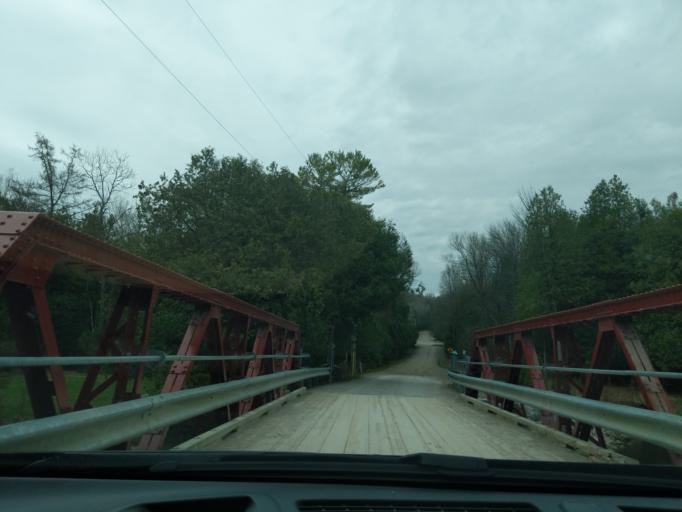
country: CA
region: Ontario
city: Orangeville
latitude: 43.9968
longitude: -80.0150
